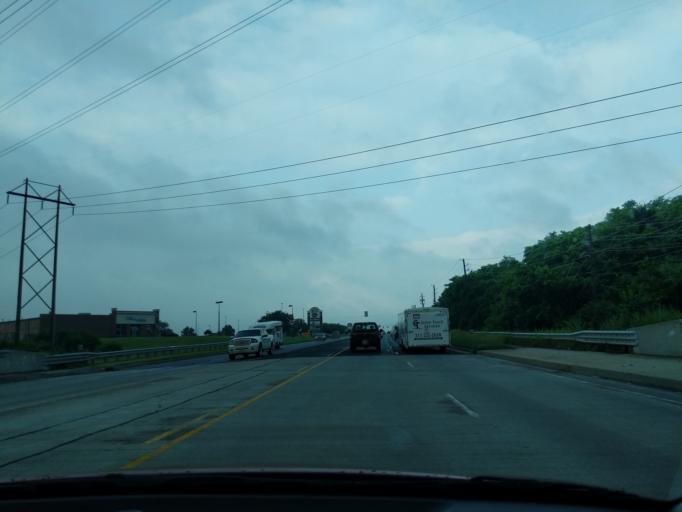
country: US
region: Indiana
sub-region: Marion County
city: Lawrence
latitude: 39.8645
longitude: -85.9687
